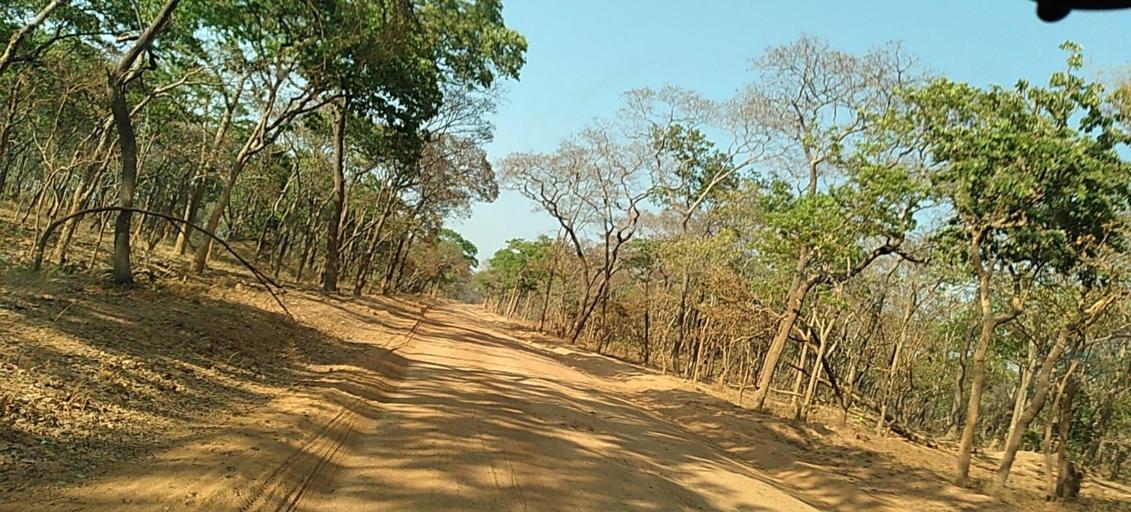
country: ZM
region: North-Western
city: Kasempa
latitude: -13.5886
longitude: 25.9852
